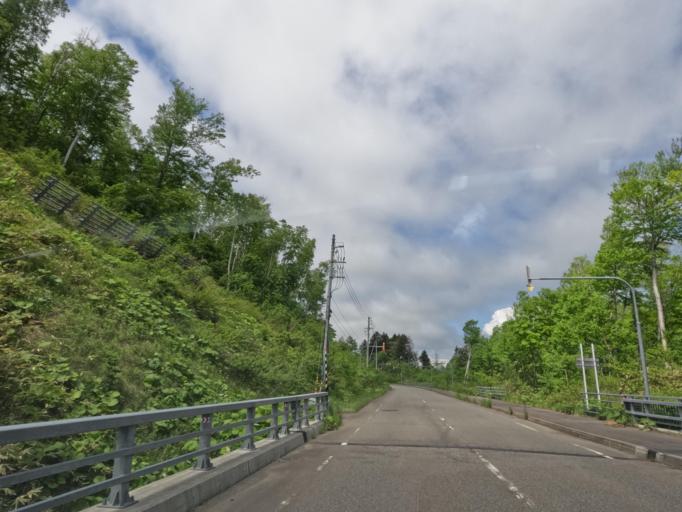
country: JP
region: Hokkaido
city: Tobetsu
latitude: 43.3390
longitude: 141.5661
